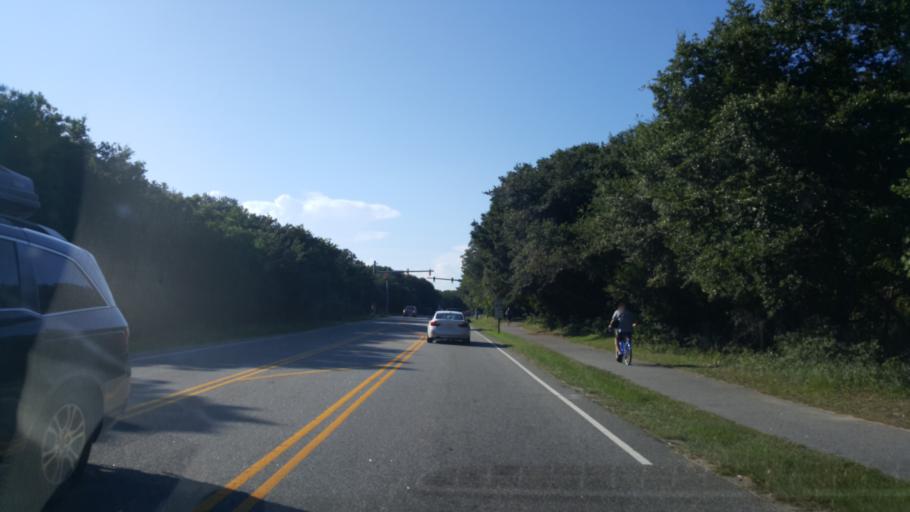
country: US
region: North Carolina
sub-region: Dare County
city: Southern Shores
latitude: 36.1434
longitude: -75.7392
